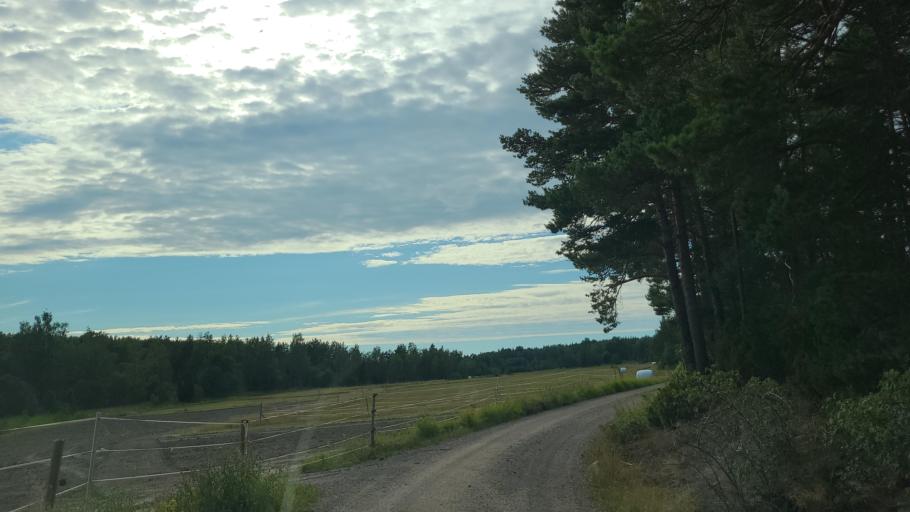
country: FI
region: Varsinais-Suomi
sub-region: Aboland-Turunmaa
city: Nagu
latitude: 60.2811
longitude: 21.9437
